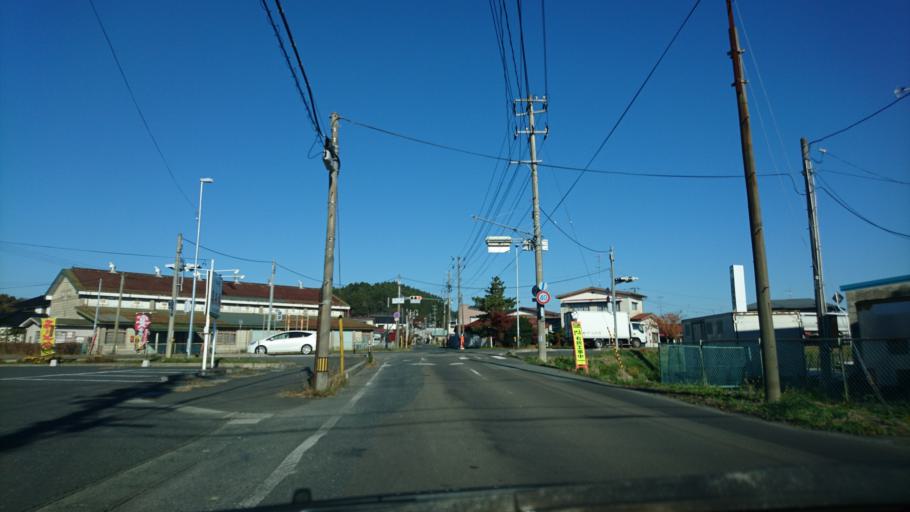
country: JP
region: Iwate
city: Mizusawa
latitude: 39.0394
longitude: 141.1222
